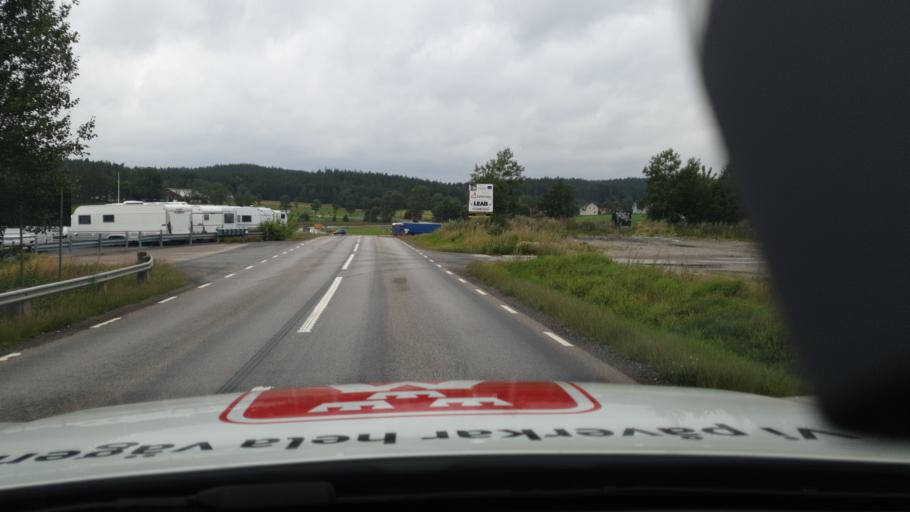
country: SE
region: Vaestra Goetaland
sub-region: Uddevalla Kommun
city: Ljungskile
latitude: 58.1883
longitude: 11.9517
